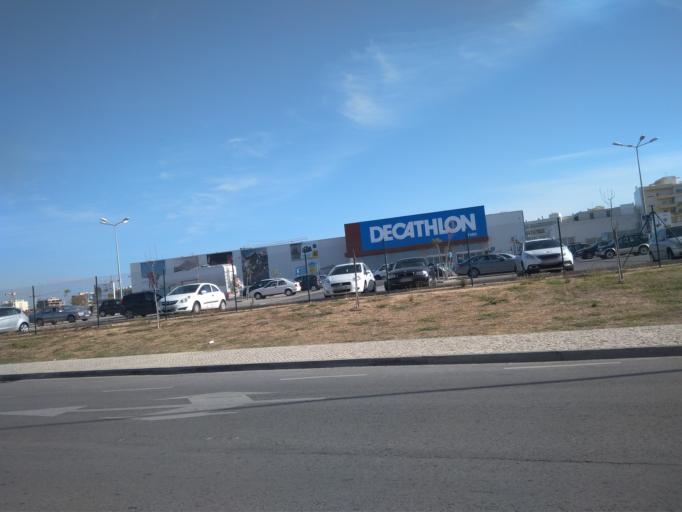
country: PT
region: Faro
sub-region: Faro
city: Faro
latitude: 37.0278
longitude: -7.9430
